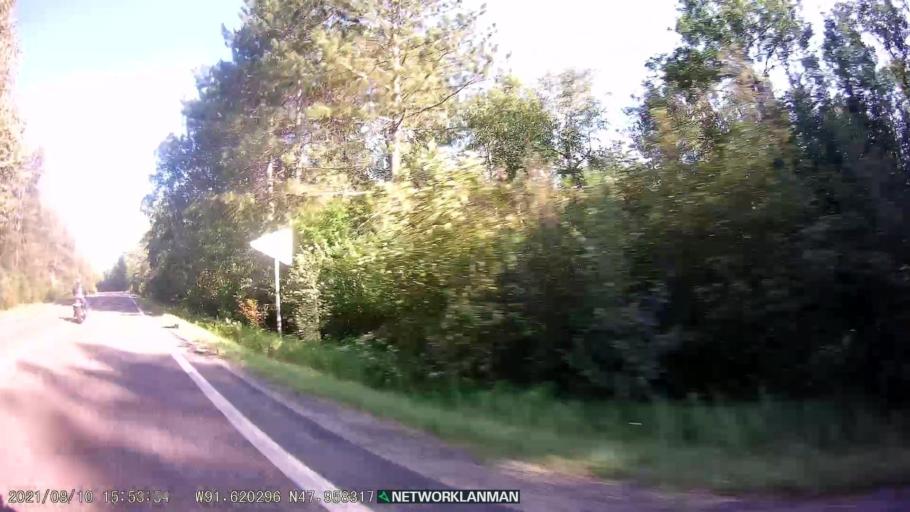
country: US
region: Minnesota
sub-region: Saint Louis County
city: Ely
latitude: 47.9582
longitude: -91.6199
